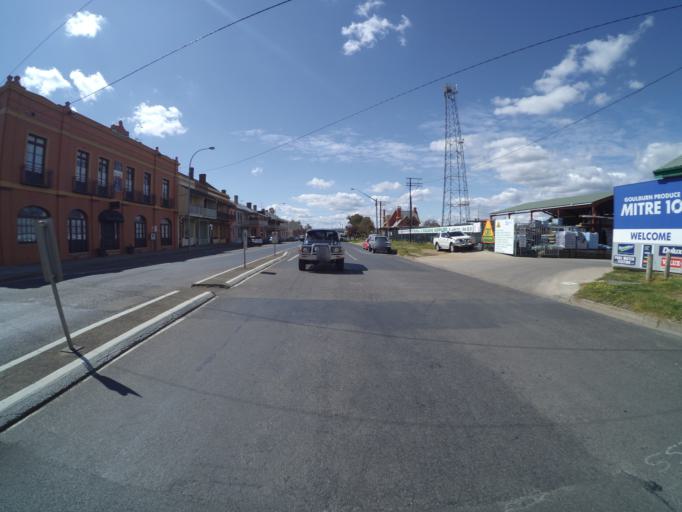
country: AU
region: New South Wales
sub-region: Goulburn Mulwaree
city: Goulburn
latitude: -34.7591
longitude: 149.7178
